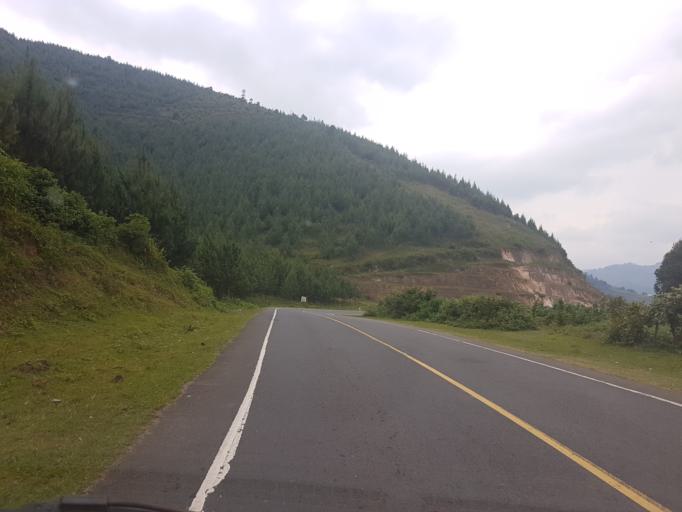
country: UG
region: Western Region
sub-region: Kabale District
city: Kabale
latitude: -1.2087
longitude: 29.8322
